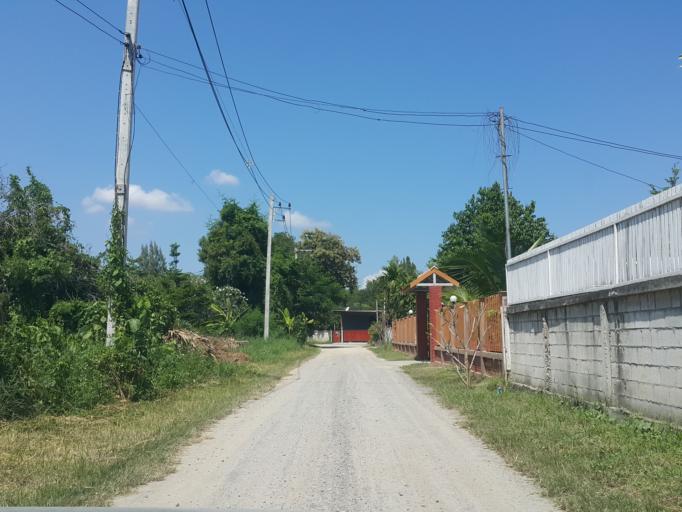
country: TH
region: Chiang Mai
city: Saraphi
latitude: 18.7615
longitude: 99.0483
